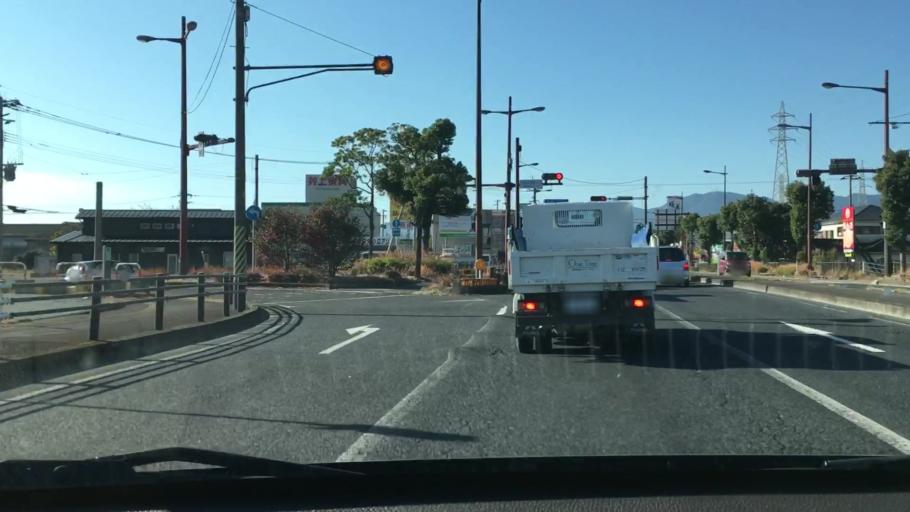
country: JP
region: Kagoshima
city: Kajiki
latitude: 31.7375
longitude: 130.6501
